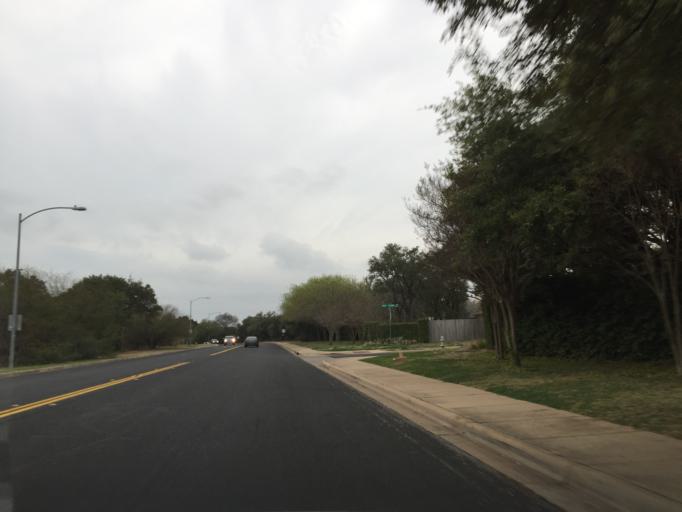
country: US
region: Texas
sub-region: Travis County
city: Rollingwood
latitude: 30.2425
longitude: -97.8285
